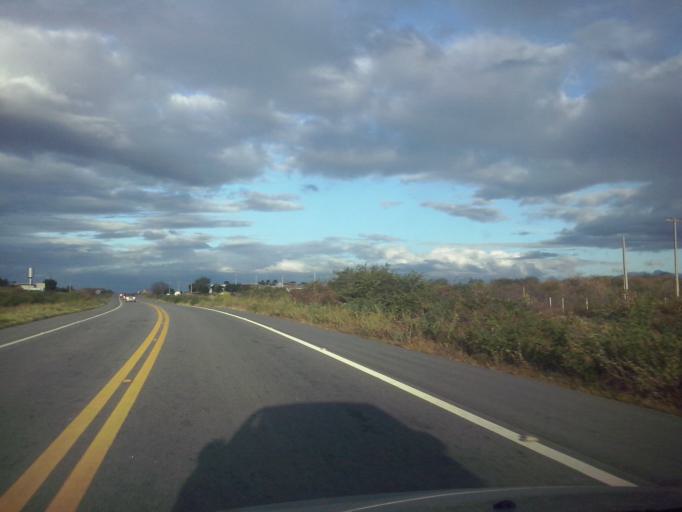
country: BR
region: Paraiba
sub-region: Patos
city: Patos
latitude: -6.9479
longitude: -37.4006
